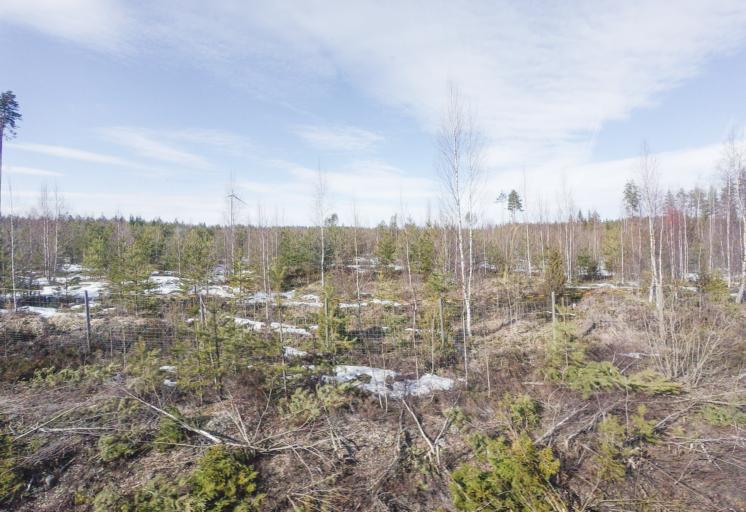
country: FI
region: South Karelia
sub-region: Lappeenranta
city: Joutseno
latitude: 61.1019
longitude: 28.4046
